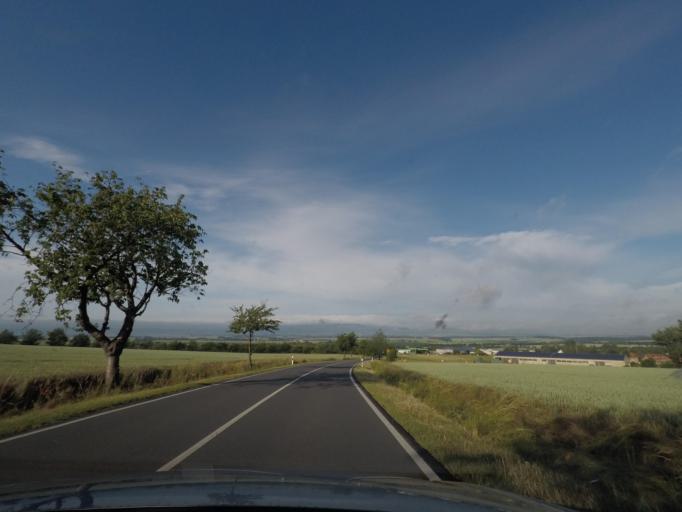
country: DE
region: Saxony-Anhalt
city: Huy-Neinstedt
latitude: 51.9745
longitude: 10.8504
